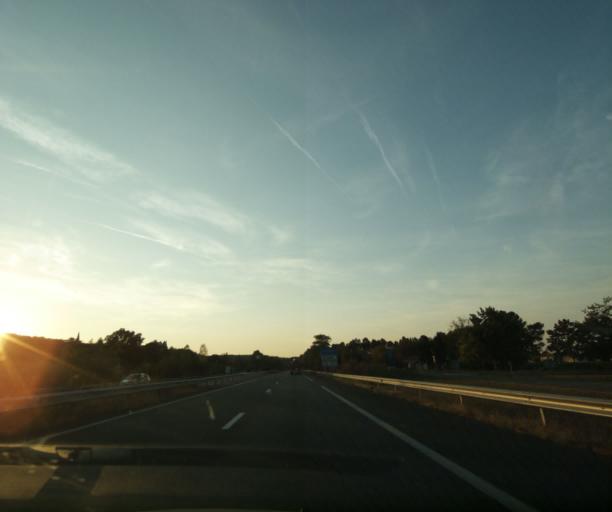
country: FR
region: Aquitaine
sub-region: Departement du Lot-et-Garonne
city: Buzet-sur-Baise
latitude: 44.2481
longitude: 0.3046
